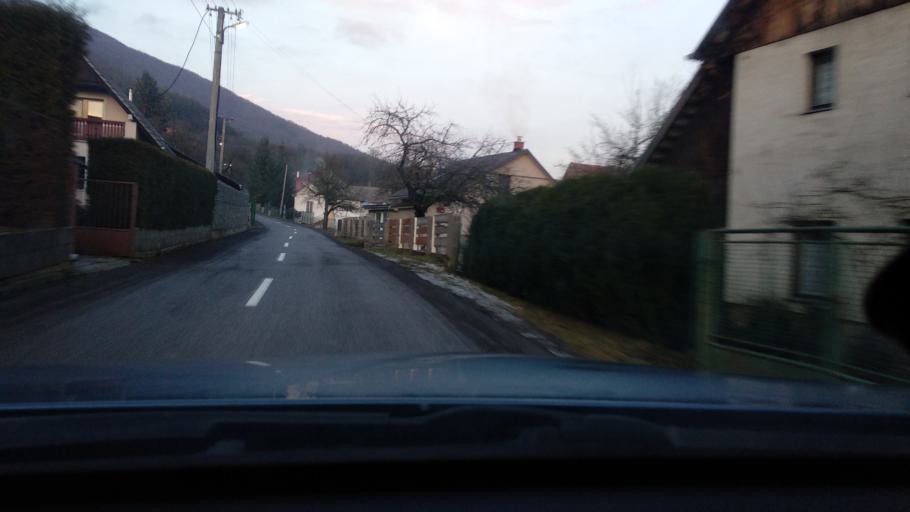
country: SK
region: Nitriansky
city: Banovce nad Bebravou
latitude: 48.8549
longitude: 18.2982
